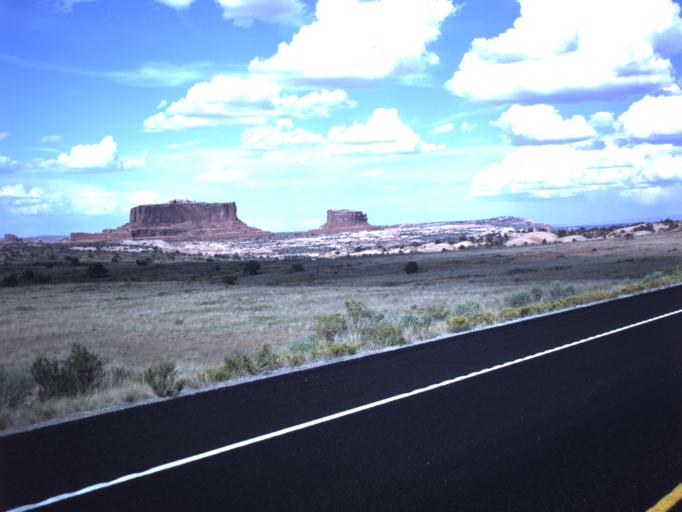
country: US
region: Utah
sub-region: Grand County
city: Moab
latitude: 38.6361
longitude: -109.7696
